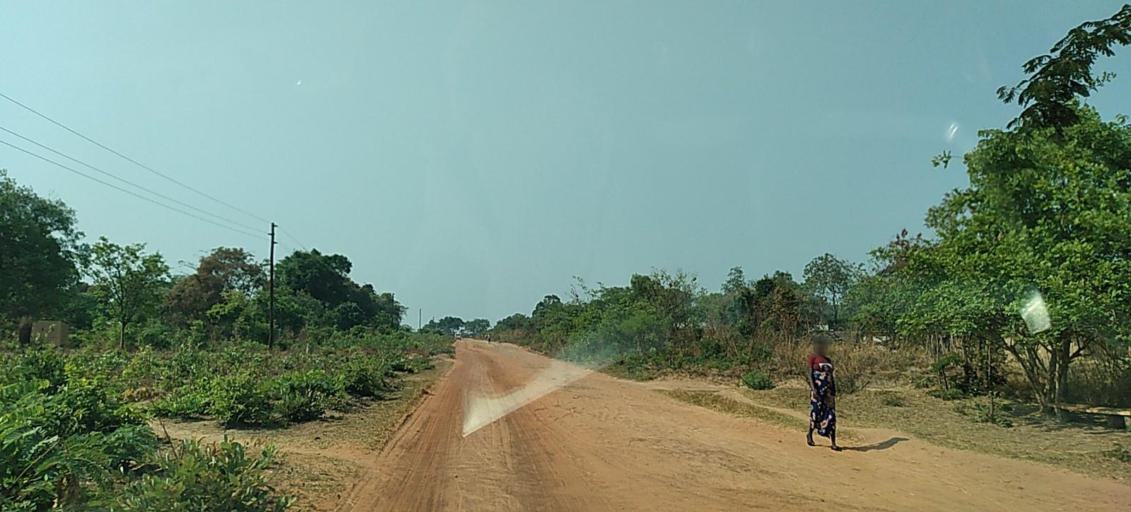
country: ZM
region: Copperbelt
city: Chingola
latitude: -12.9174
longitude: 27.3732
